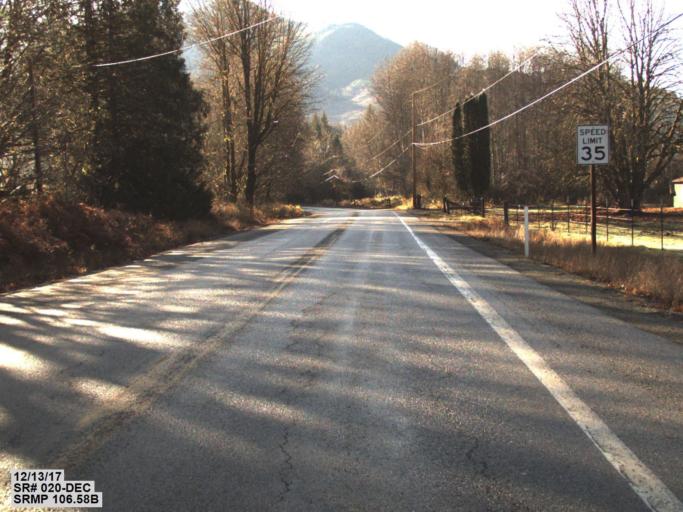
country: US
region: Washington
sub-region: Snohomish County
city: Darrington
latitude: 48.5334
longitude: -121.4303
